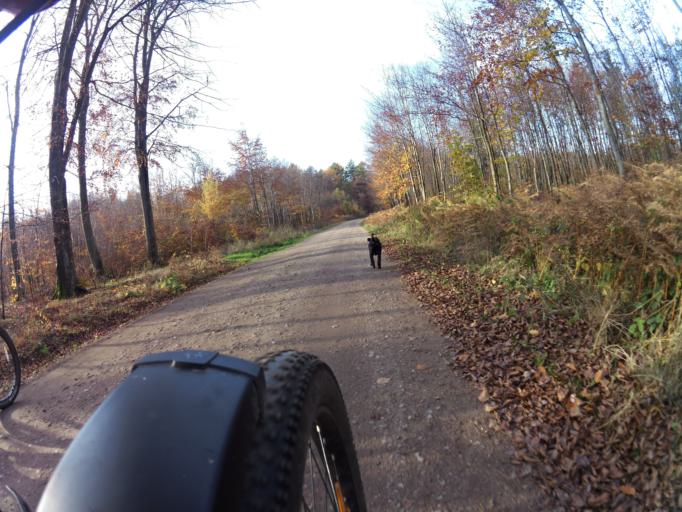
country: PL
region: Pomeranian Voivodeship
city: Strzelno
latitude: 54.7397
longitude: 18.2616
